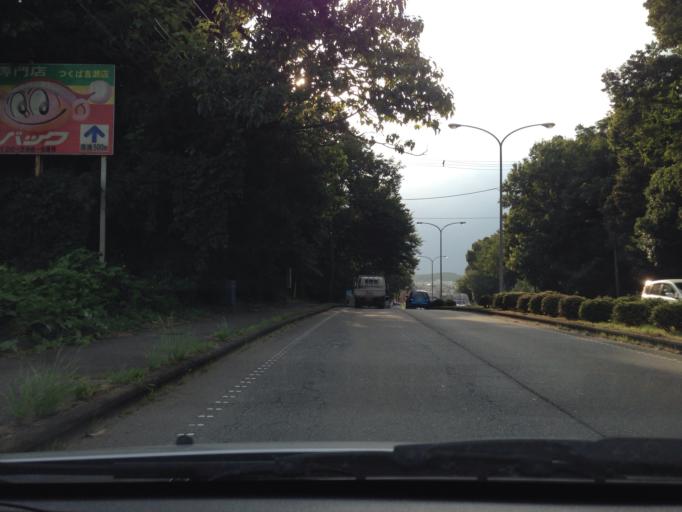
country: JP
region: Ibaraki
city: Naka
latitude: 36.0859
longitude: 140.1558
